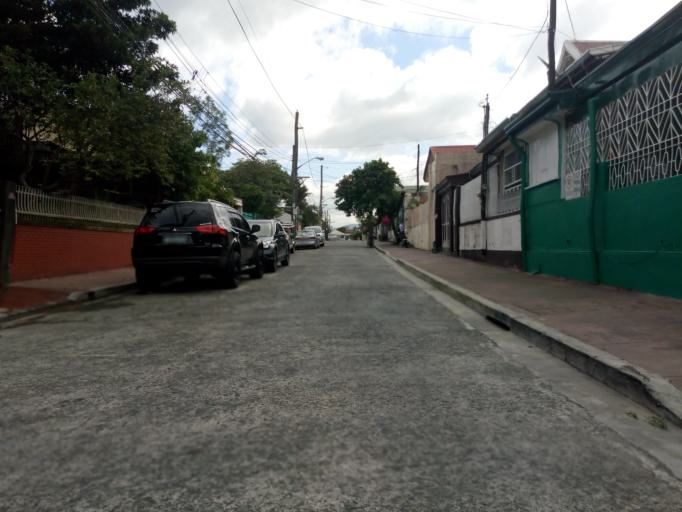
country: PH
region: Calabarzon
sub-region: Province of Rizal
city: Antipolo
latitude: 14.6395
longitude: 121.1182
